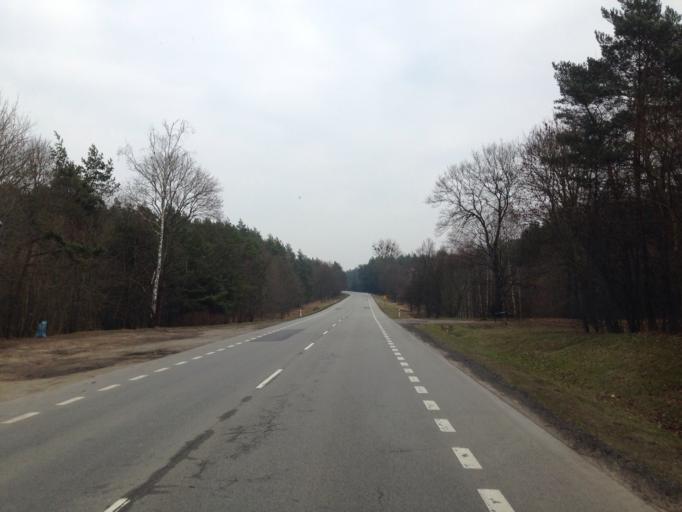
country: PL
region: Pomeranian Voivodeship
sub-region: Powiat tczewski
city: Gniew
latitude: 53.8165
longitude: 18.8034
